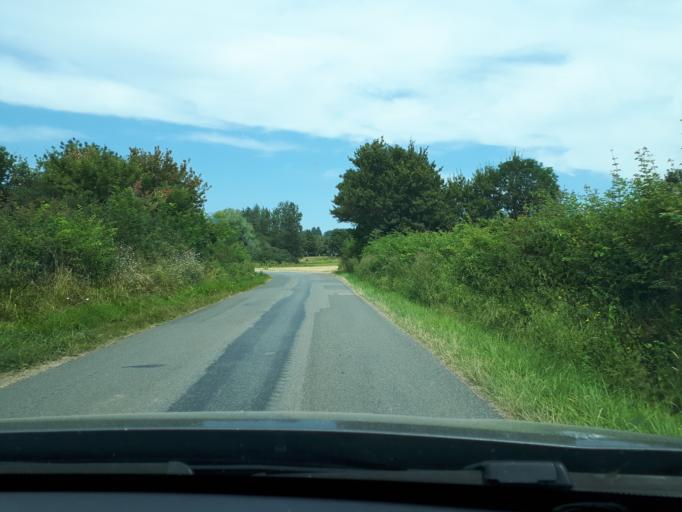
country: FR
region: Centre
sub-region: Departement du Cher
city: Sancerre
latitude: 47.3004
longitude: 2.7477
